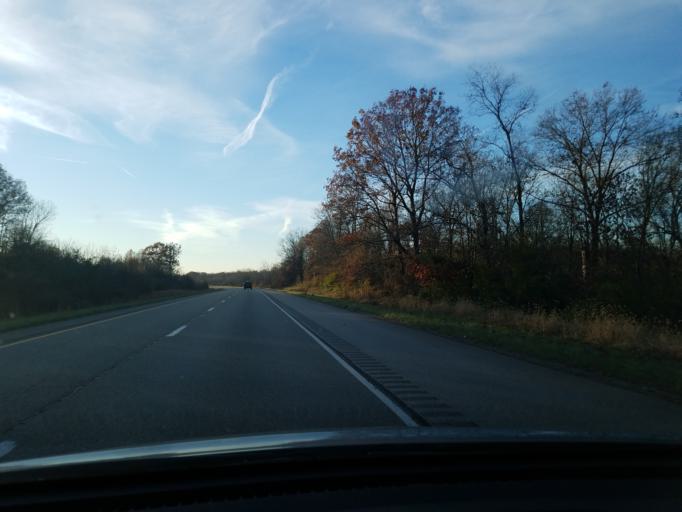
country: US
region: Indiana
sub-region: Warrick County
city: Boonville
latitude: 38.2015
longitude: -87.2321
